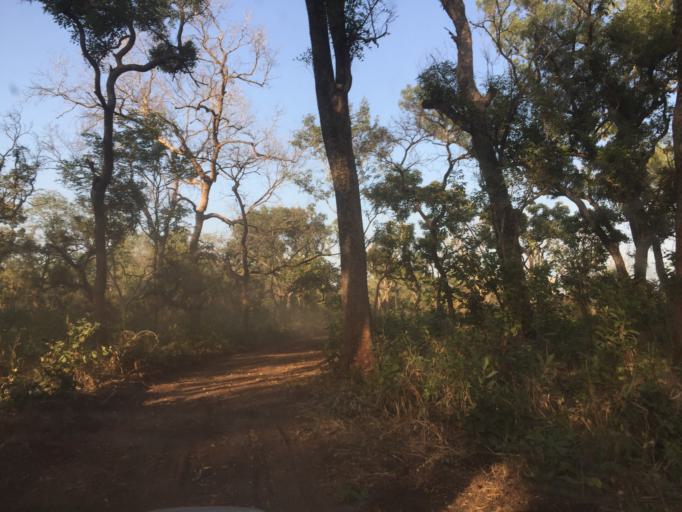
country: GW
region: Oio
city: Farim
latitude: 12.5280
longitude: -15.2788
